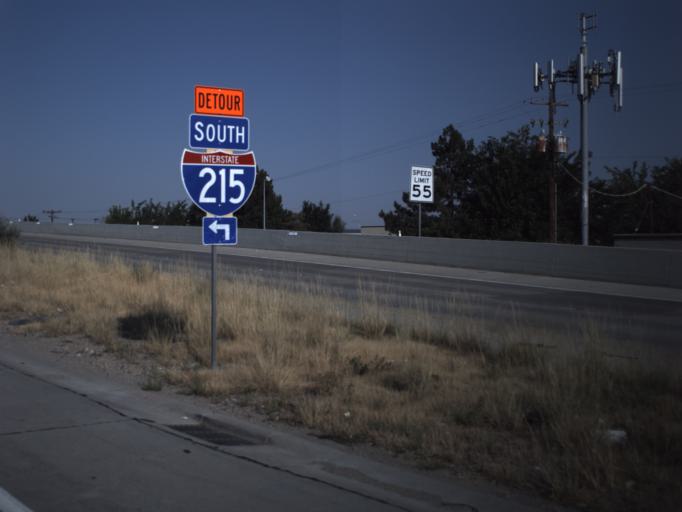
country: US
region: Utah
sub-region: Salt Lake County
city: South Salt Lake
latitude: 40.7245
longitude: -111.9362
